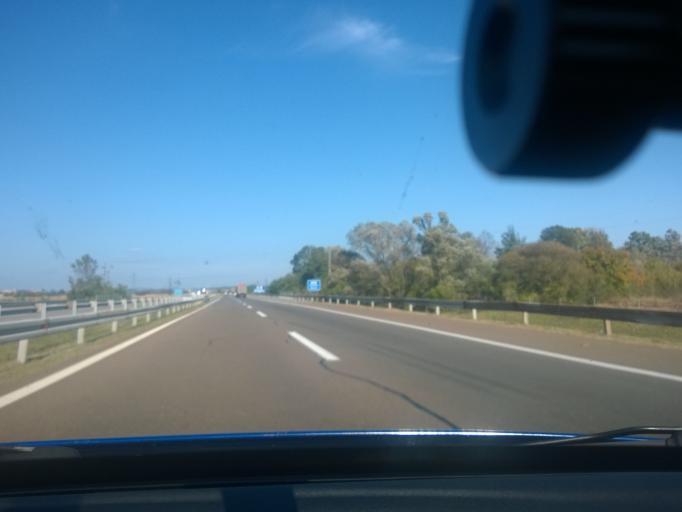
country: RS
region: Central Serbia
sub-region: Pomoravski Okrug
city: Cuprija
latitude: 43.9238
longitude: 21.3922
